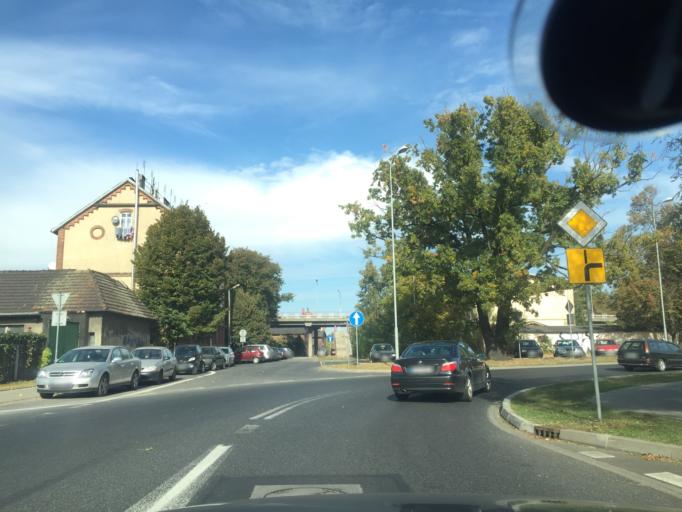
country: PL
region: Greater Poland Voivodeship
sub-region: Powiat wrzesinski
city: Wrzesnia
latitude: 52.3290
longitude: 17.5562
